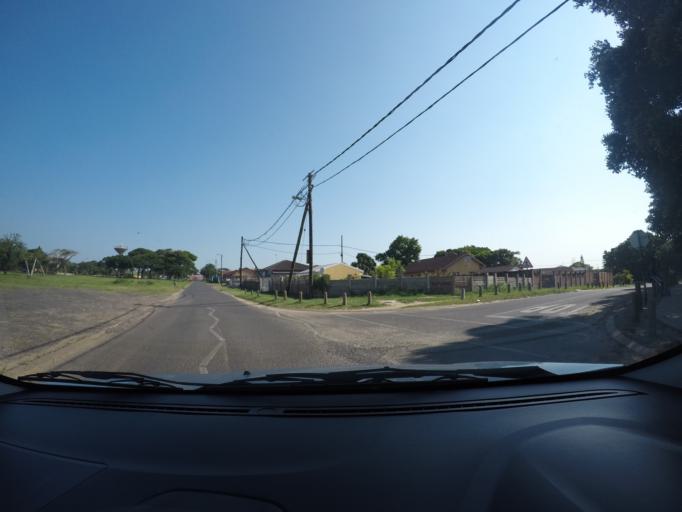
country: ZA
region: KwaZulu-Natal
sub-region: uThungulu District Municipality
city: Richards Bay
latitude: -28.7199
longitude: 32.0396
